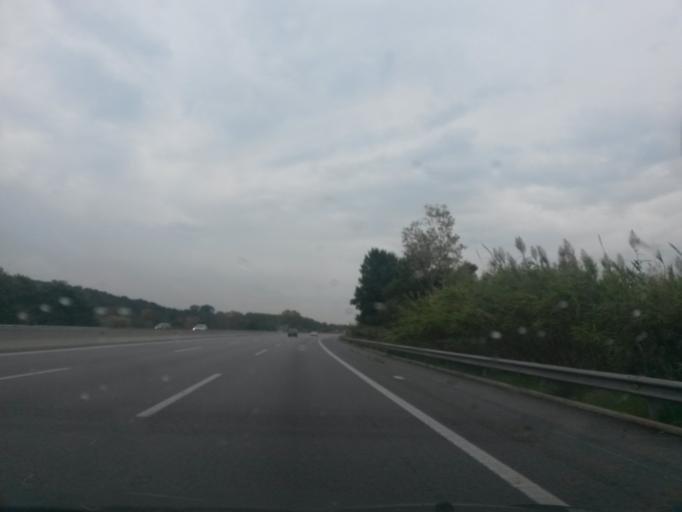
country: ES
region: Catalonia
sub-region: Provincia de Barcelona
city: Llinars del Valles
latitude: 41.6298
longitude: 2.3837
